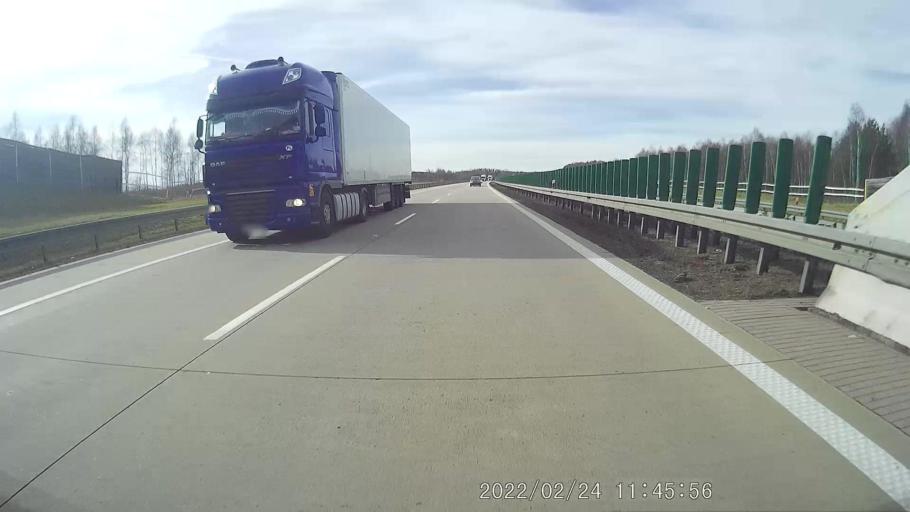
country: PL
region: Lower Silesian Voivodeship
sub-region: Powiat polkowicki
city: Radwanice
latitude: 51.5660
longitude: 15.9406
